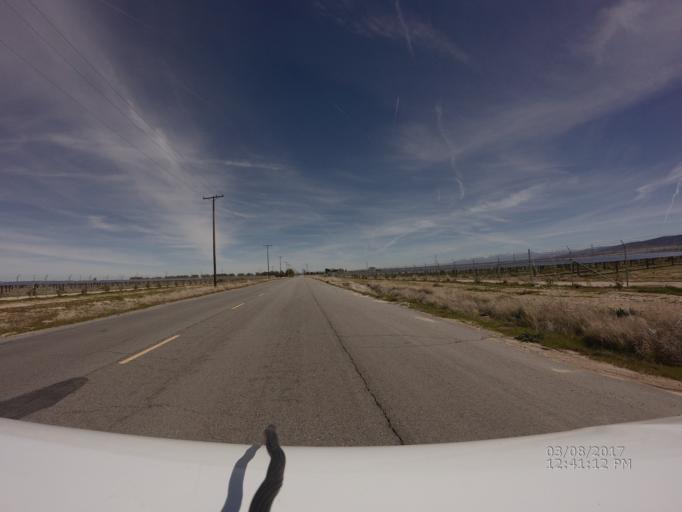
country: US
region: California
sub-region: Los Angeles County
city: Leona Valley
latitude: 34.7037
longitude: -118.3054
